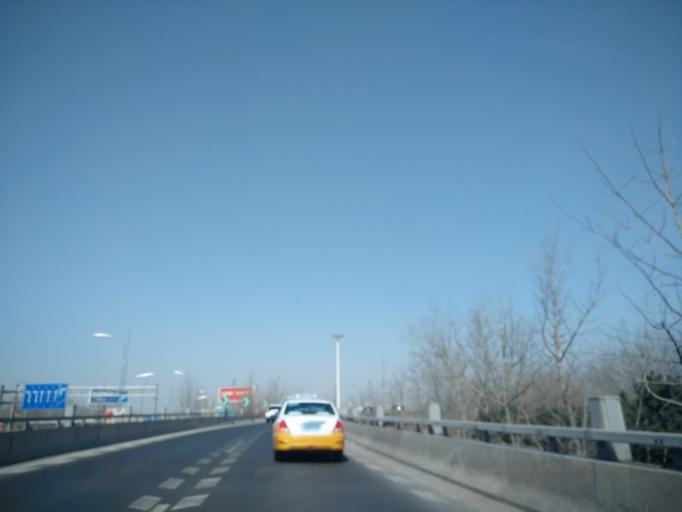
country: CN
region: Beijing
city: Jiugong
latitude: 39.8123
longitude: 116.4875
